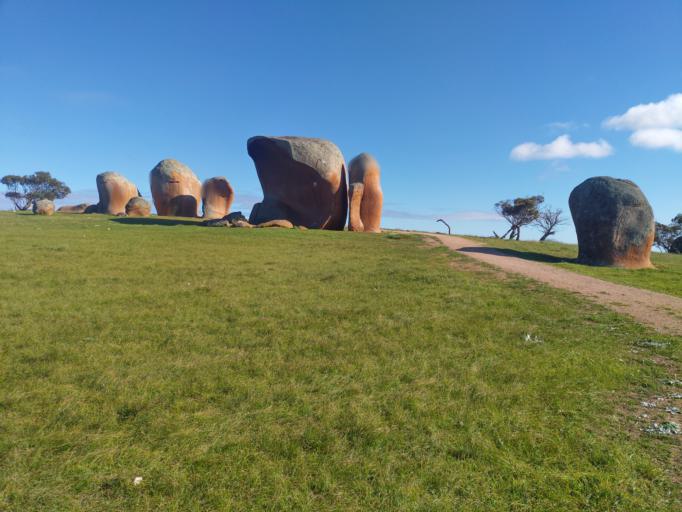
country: AU
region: South Australia
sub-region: Streaky Bay
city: Streaky Bay
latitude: -33.0156
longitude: 134.4918
